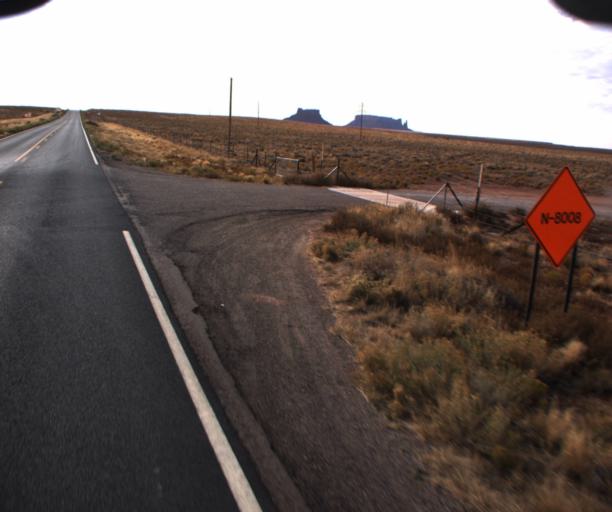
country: US
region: Arizona
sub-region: Apache County
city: Many Farms
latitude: 36.5885
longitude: -109.5606
